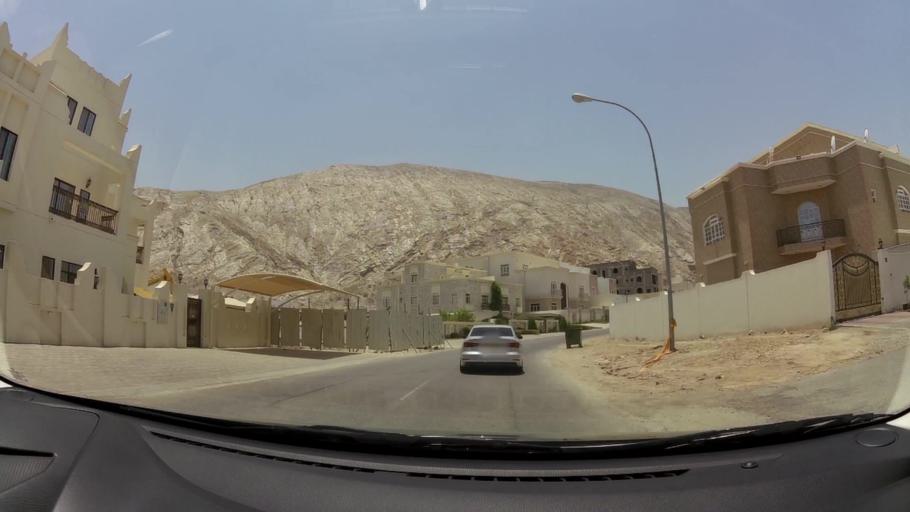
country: OM
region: Muhafazat Masqat
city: Bawshar
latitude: 23.5599
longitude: 58.4176
